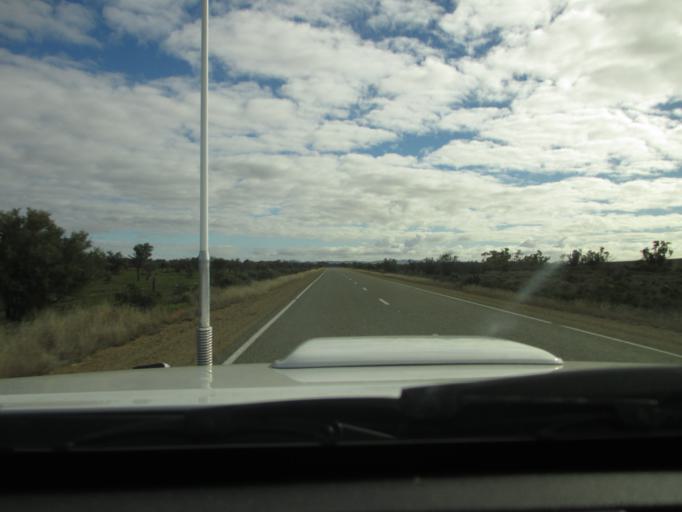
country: AU
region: South Australia
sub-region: Flinders Ranges
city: Quorn
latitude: -32.3843
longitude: 138.5024
